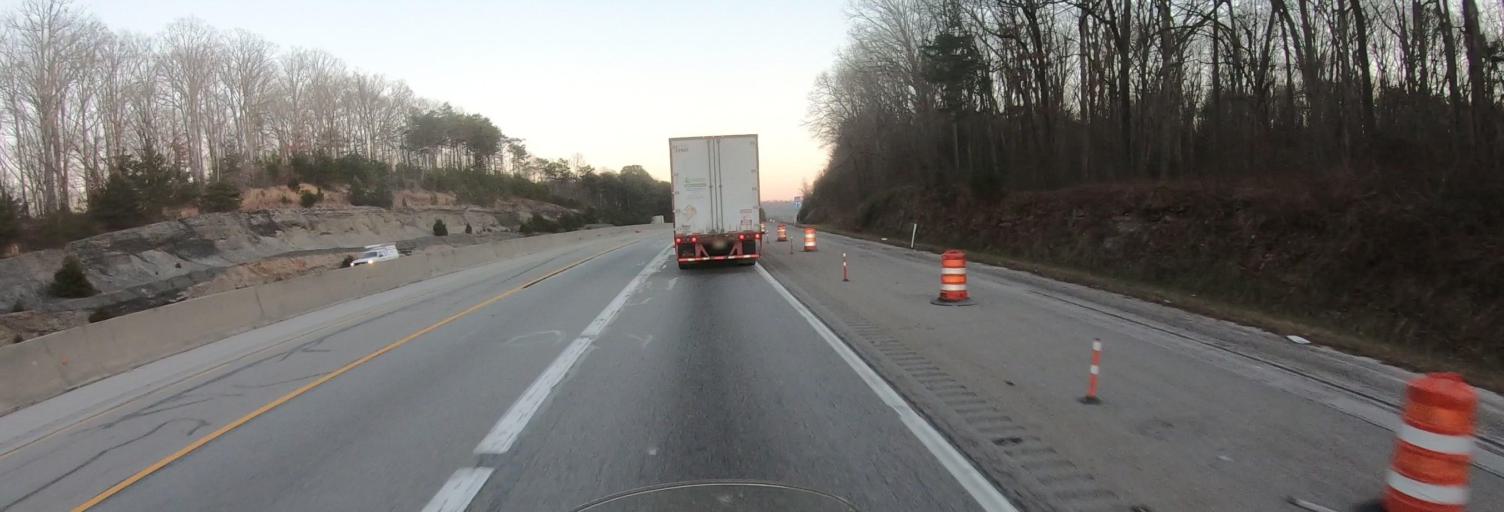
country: US
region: Kentucky
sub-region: Laurel County
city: London
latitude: 37.2213
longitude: -84.2072
